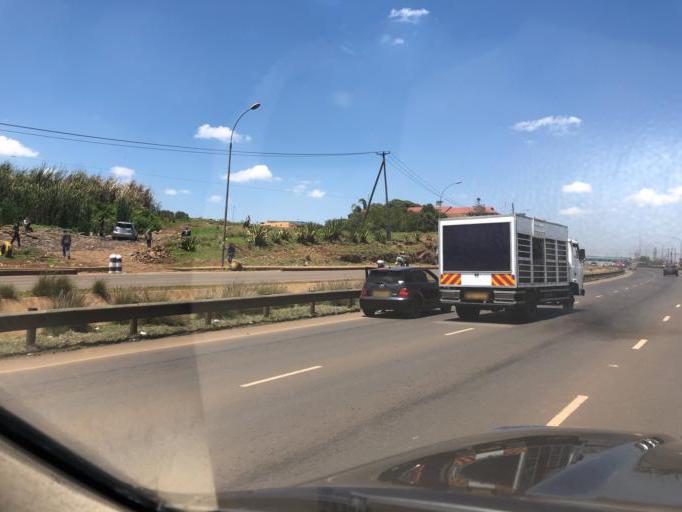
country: KE
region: Kiambu
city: Kiambu
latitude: -1.2140
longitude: 36.8984
